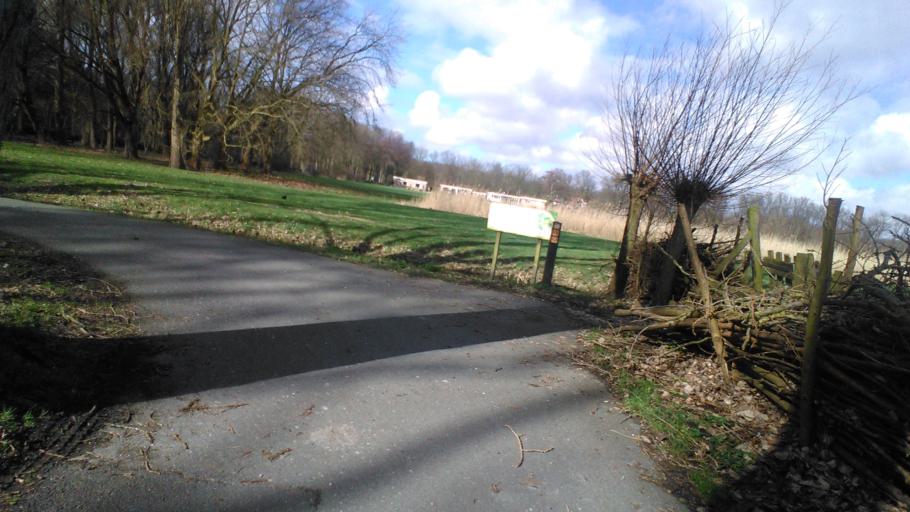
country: NL
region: South Holland
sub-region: Gemeente Delft
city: Delft
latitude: 52.0155
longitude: 4.3805
